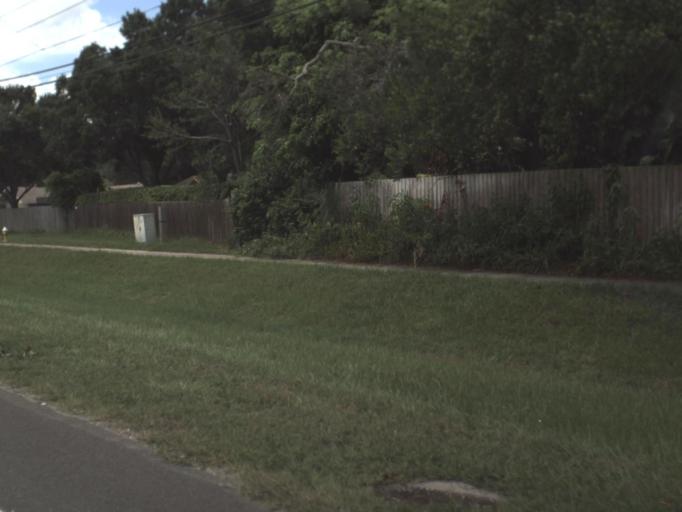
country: US
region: Florida
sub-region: Pinellas County
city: Safety Harbor
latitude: 28.0074
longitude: -82.7091
